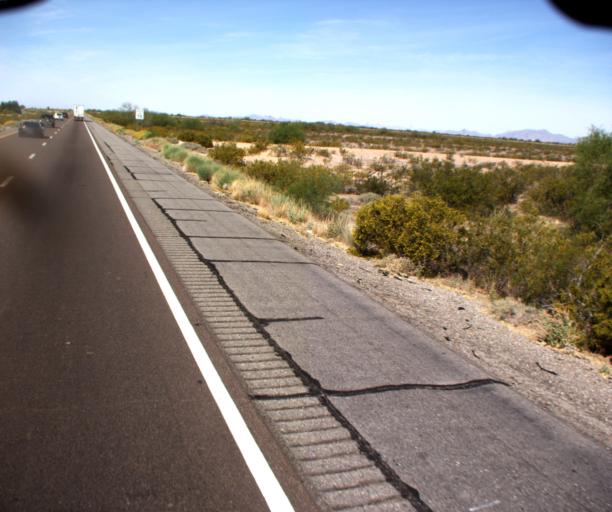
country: US
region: Arizona
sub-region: La Paz County
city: Salome
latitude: 33.5558
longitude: -113.2638
